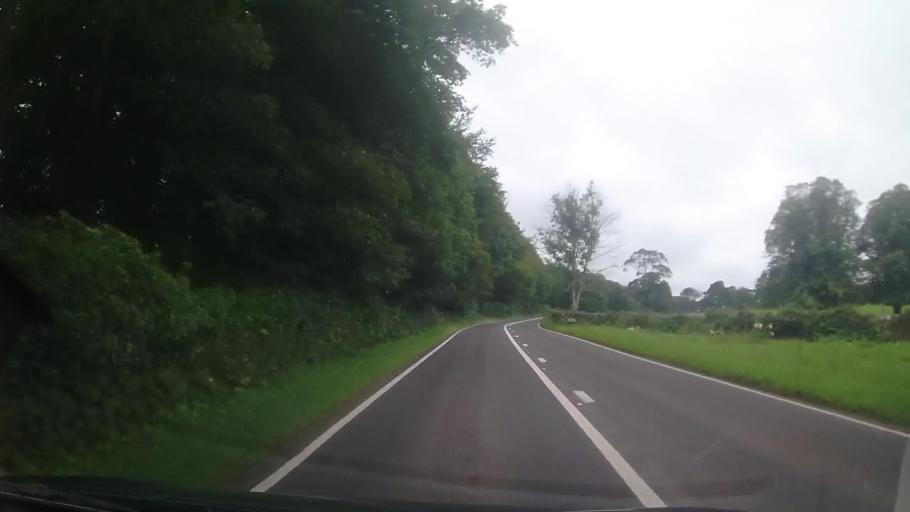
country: GB
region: Wales
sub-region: Gwynedd
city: Y Felinheli
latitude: 53.2030
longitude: -4.2229
